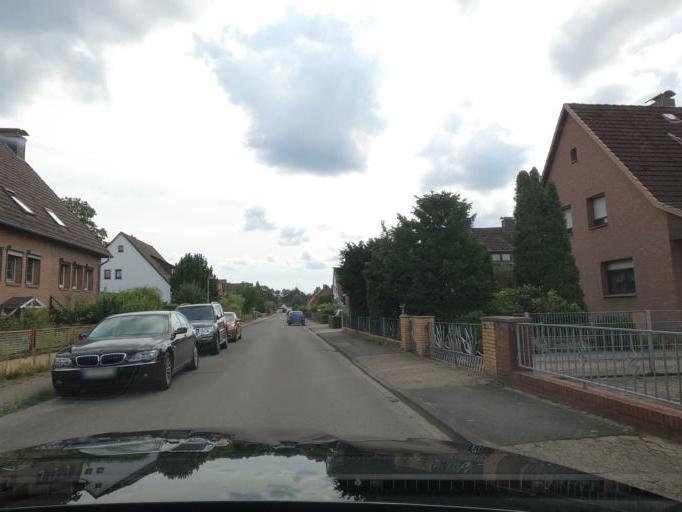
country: DE
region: Lower Saxony
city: Isernhagen Farster Bauerschaft
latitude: 52.5182
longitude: 9.9176
